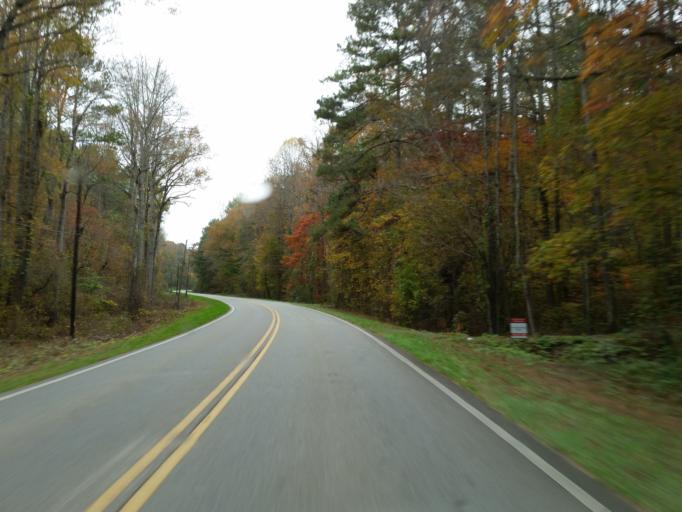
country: US
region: Georgia
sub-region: Pickens County
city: Jasper
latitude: 34.4886
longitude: -84.4226
